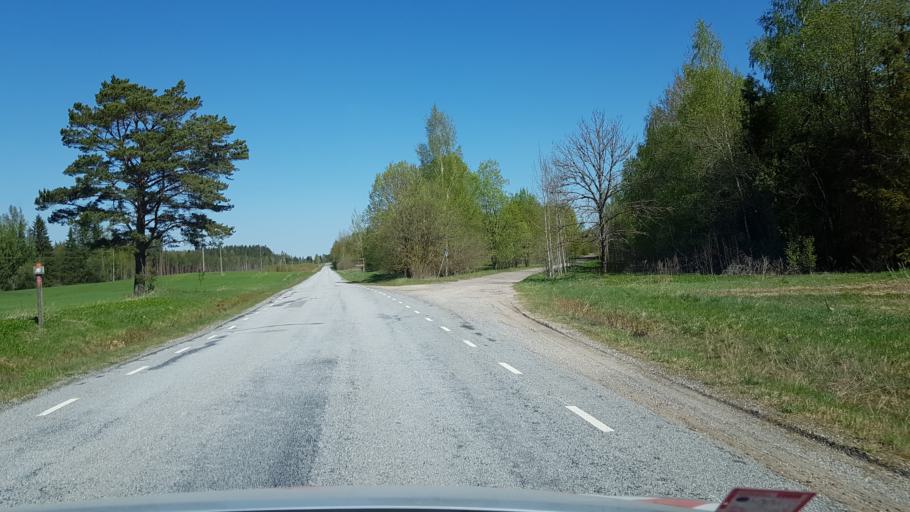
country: EE
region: Vorumaa
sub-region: Voru linn
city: Voru
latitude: 57.9297
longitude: 26.9515
